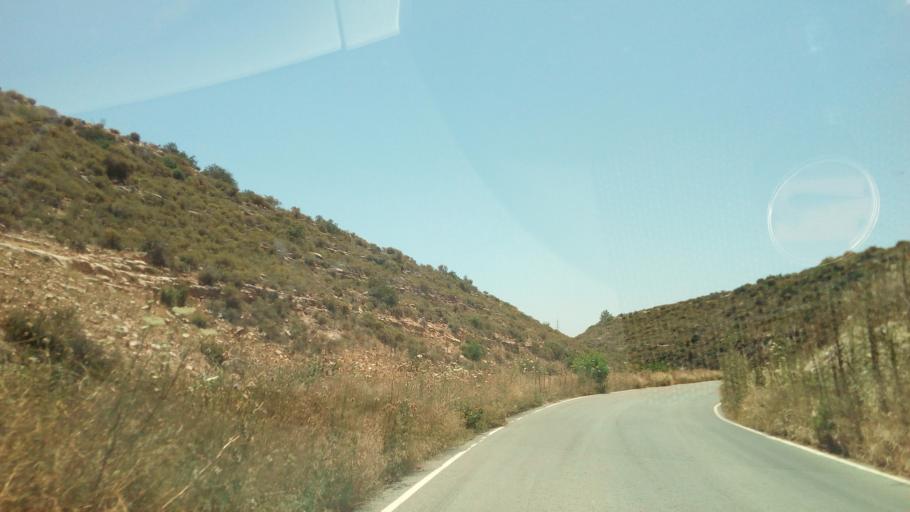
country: CY
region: Limassol
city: Ypsonas
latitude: 34.7267
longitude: 32.9509
